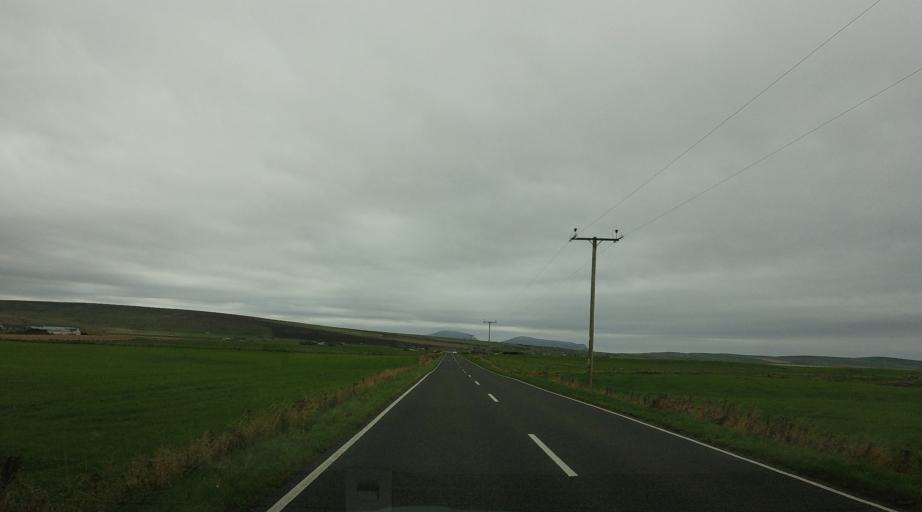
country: GB
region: Scotland
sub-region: Orkney Islands
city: Stromness
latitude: 58.9987
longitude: -3.1789
